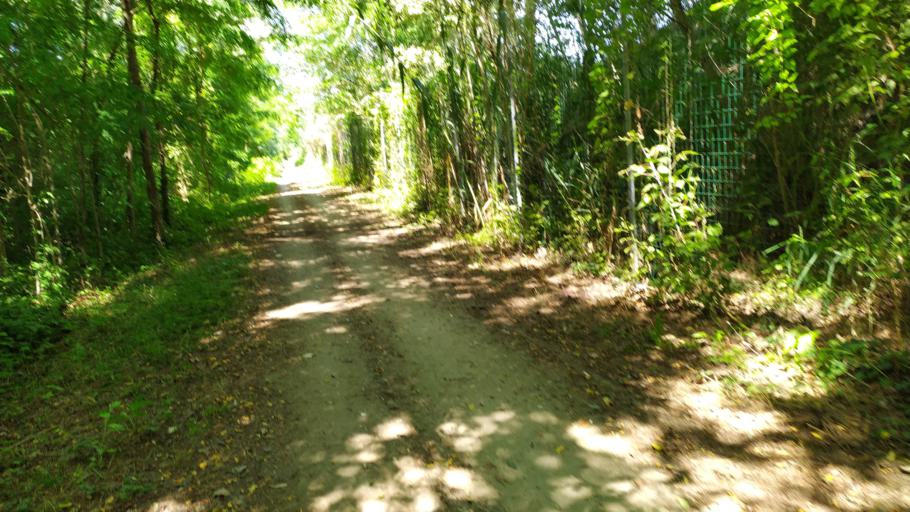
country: IT
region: Emilia-Romagna
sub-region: Forli-Cesena
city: Castrocaro Terme e Terra del Sole
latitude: 44.2033
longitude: 12.0059
